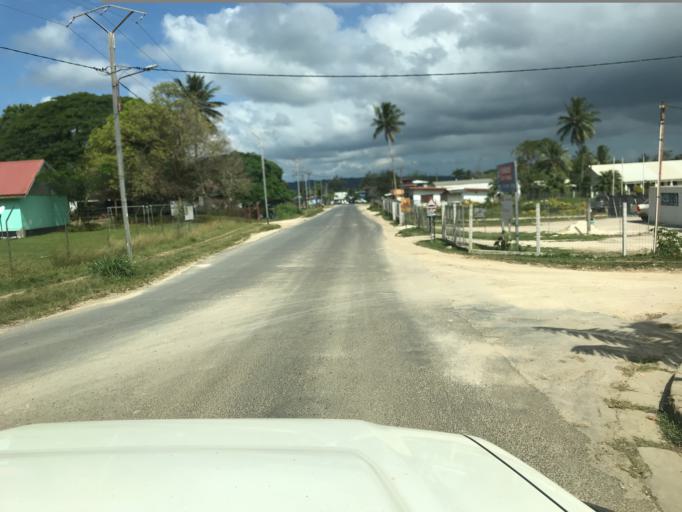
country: VU
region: Sanma
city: Luganville
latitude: -15.5107
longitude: 167.1775
